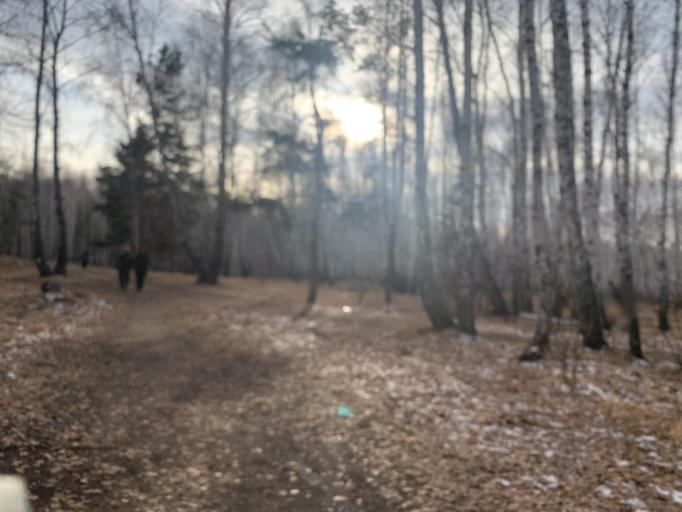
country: RU
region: Chelyabinsk
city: Roshchino
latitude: 55.2034
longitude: 61.3041
